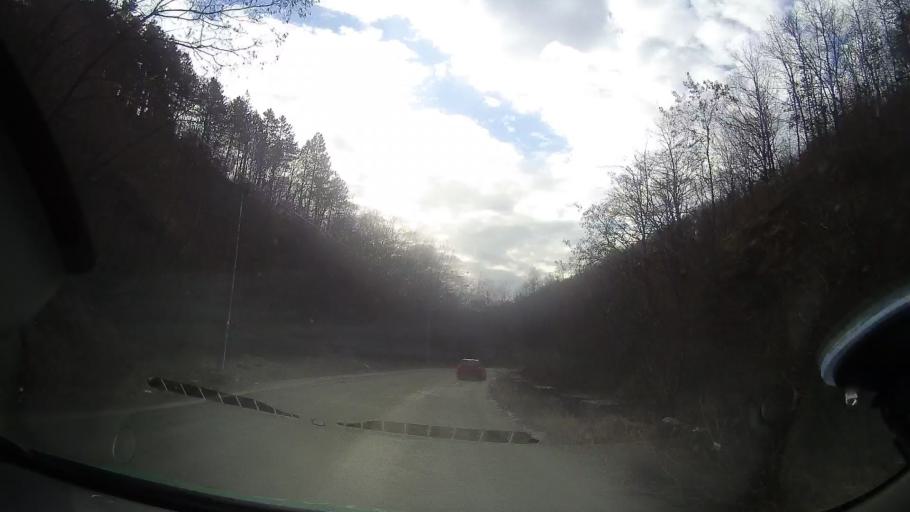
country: RO
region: Cluj
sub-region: Comuna Baisoara
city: Baisoara
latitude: 46.5886
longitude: 23.4585
